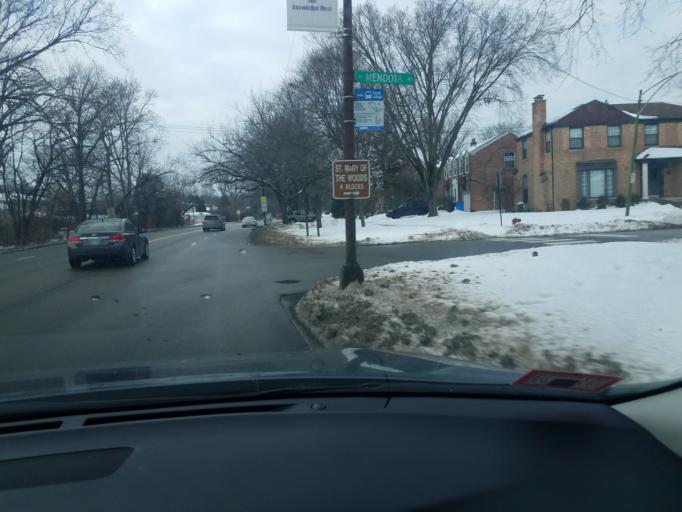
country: US
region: Illinois
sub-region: Cook County
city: Niles
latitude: 42.0047
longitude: -87.7822
